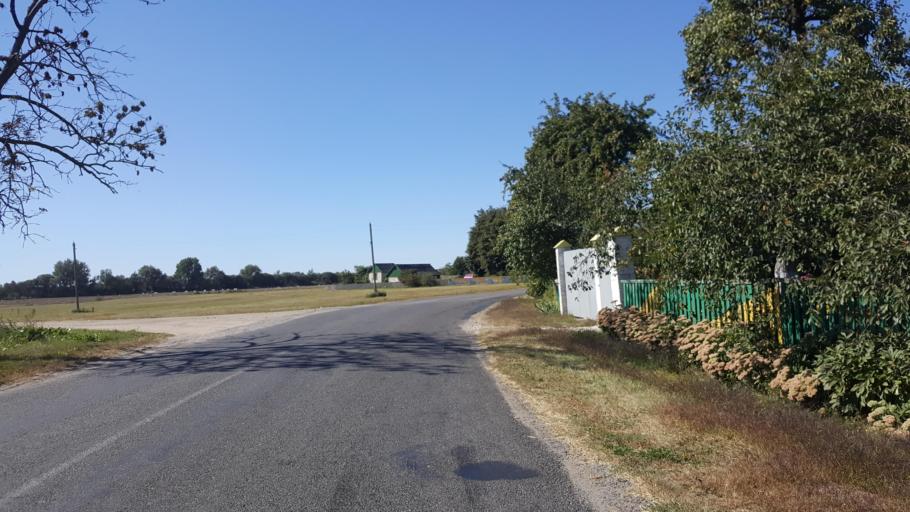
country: PL
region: Lublin Voivodeship
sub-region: Powiat bialski
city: Terespol
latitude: 52.2594
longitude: 23.5456
